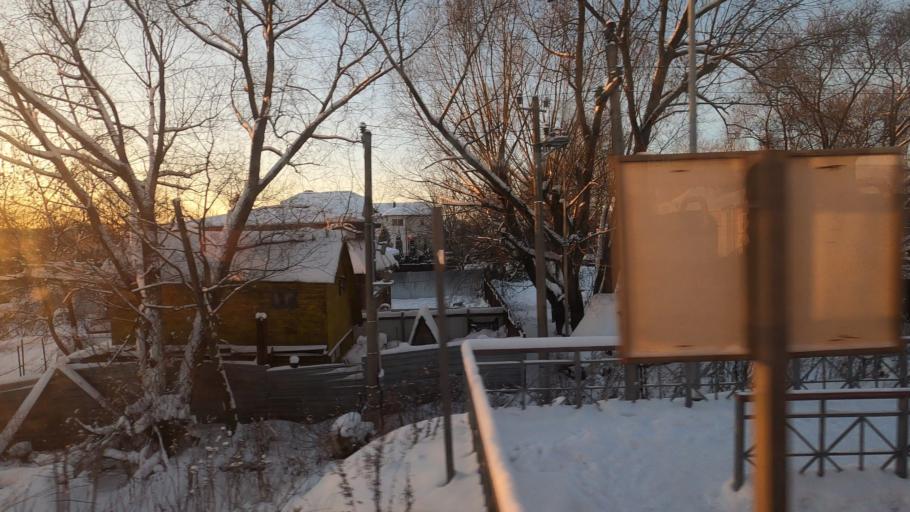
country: RU
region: Moskovskaya
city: Dmitrov
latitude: 56.3480
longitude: 37.5157
